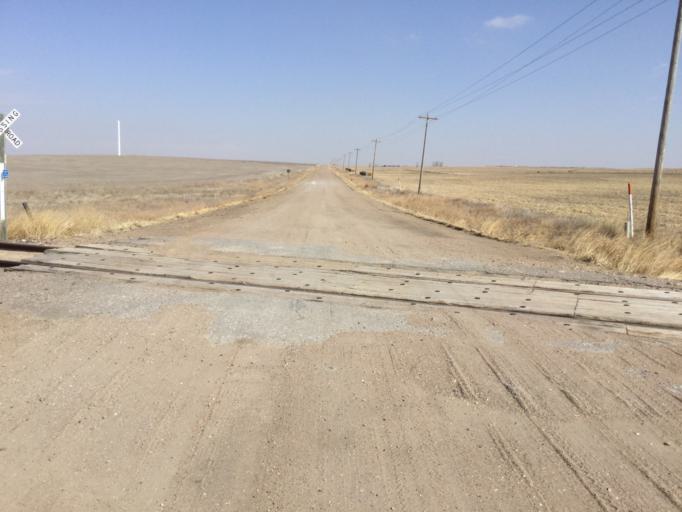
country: US
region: Kansas
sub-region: Rush County
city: La Crosse
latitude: 38.5540
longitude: -99.4386
